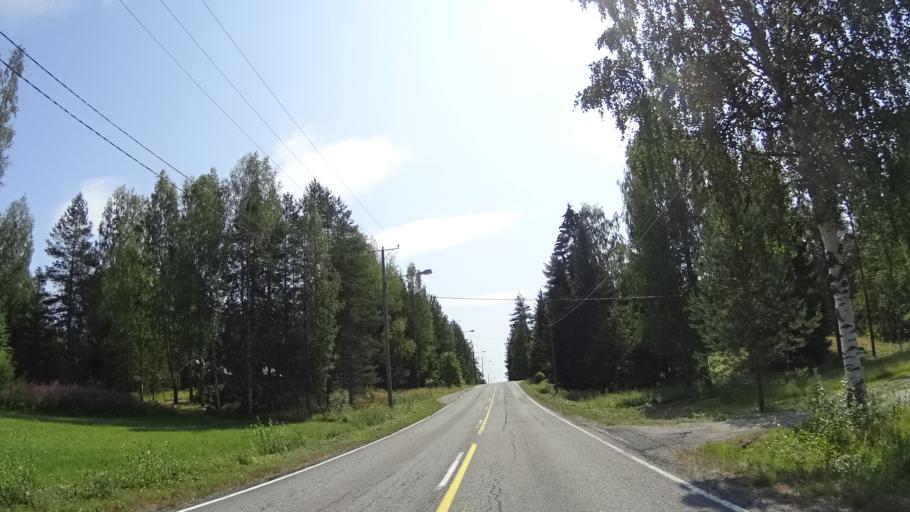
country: FI
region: Pirkanmaa
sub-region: Ylae-Pirkanmaa
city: Maenttae
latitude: 61.9028
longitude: 24.7901
